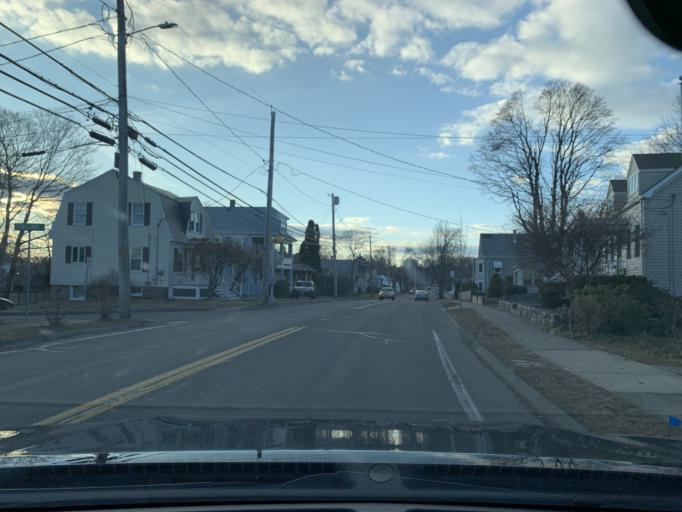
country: US
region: Massachusetts
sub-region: Essex County
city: Danvers
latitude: 42.5652
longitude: -70.9440
